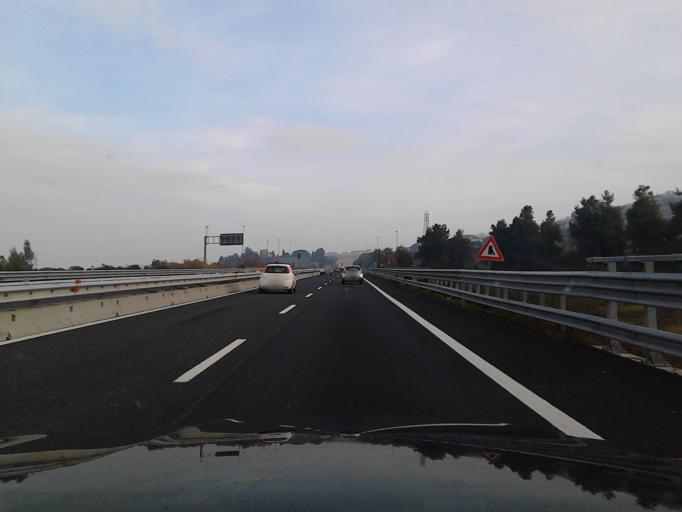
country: IT
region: Abruzzo
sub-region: Provincia di Teramo
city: Borgo Santa Maria Immacolata
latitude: 42.6067
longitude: 14.0471
